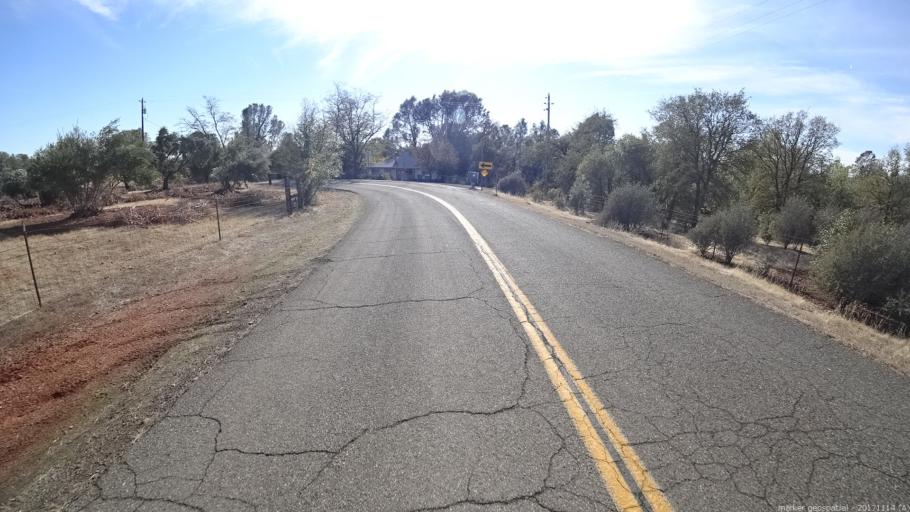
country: US
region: California
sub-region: Shasta County
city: Anderson
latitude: 40.4325
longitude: -122.4264
